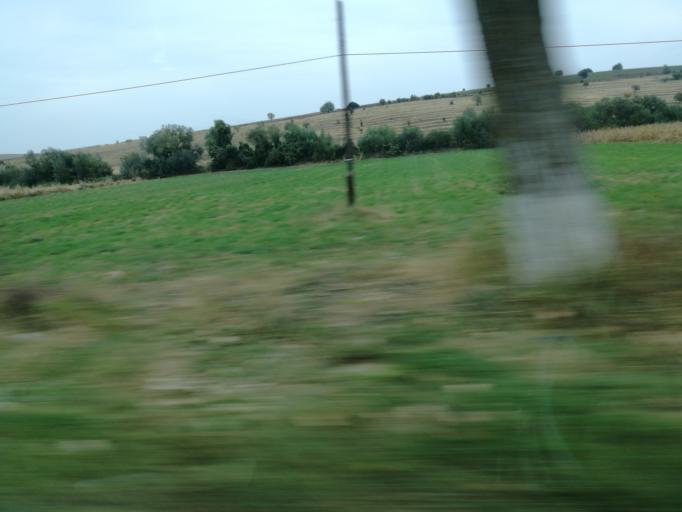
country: RO
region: Tulcea
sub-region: Comuna Ciucurova
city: Ciucurova
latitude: 44.9230
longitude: 28.4522
